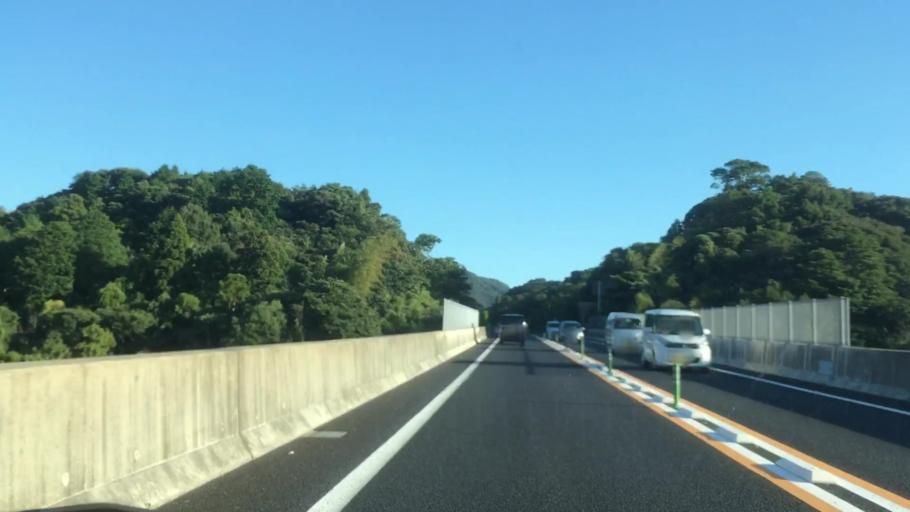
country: JP
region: Nagasaki
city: Sasebo
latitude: 33.1957
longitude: 129.6787
